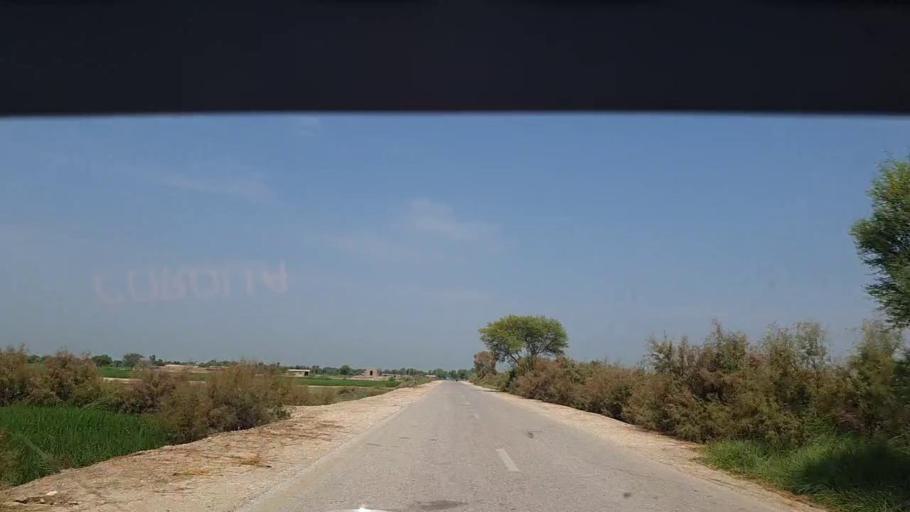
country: PK
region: Sindh
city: Thul
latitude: 28.1362
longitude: 68.8175
